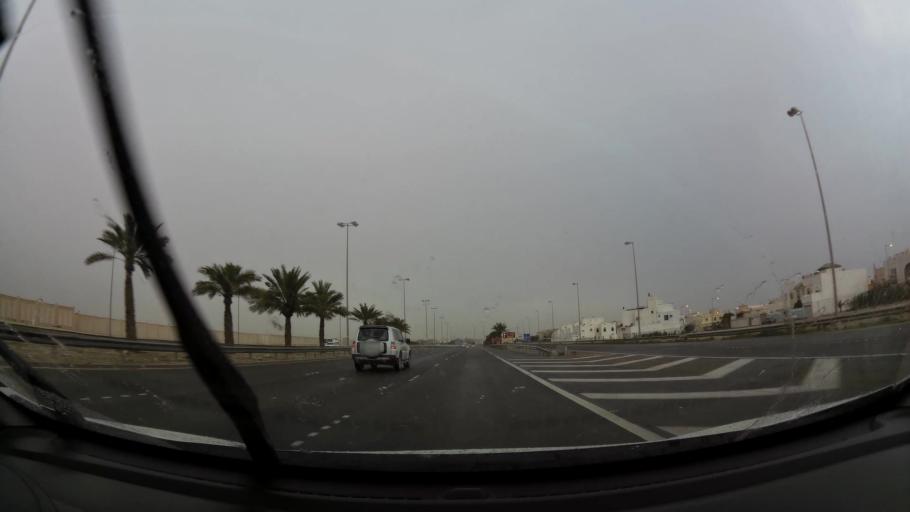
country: BH
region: Central Governorate
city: Madinat Hamad
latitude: 26.1035
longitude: 50.5110
